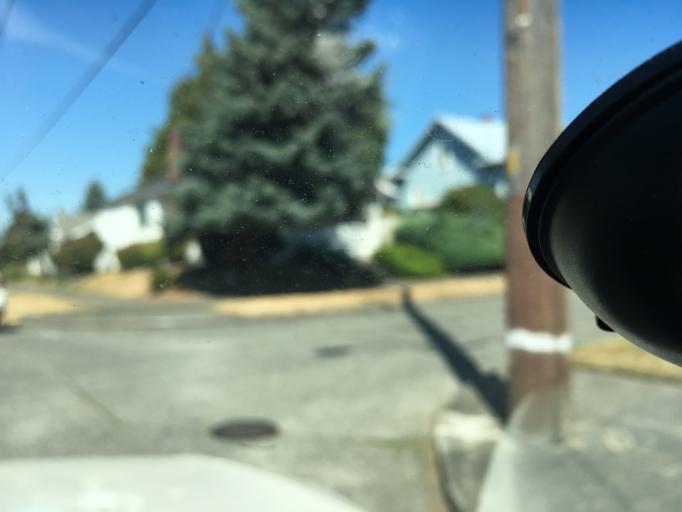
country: US
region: Washington
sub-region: King County
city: Shoreline
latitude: 47.6883
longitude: -122.3579
